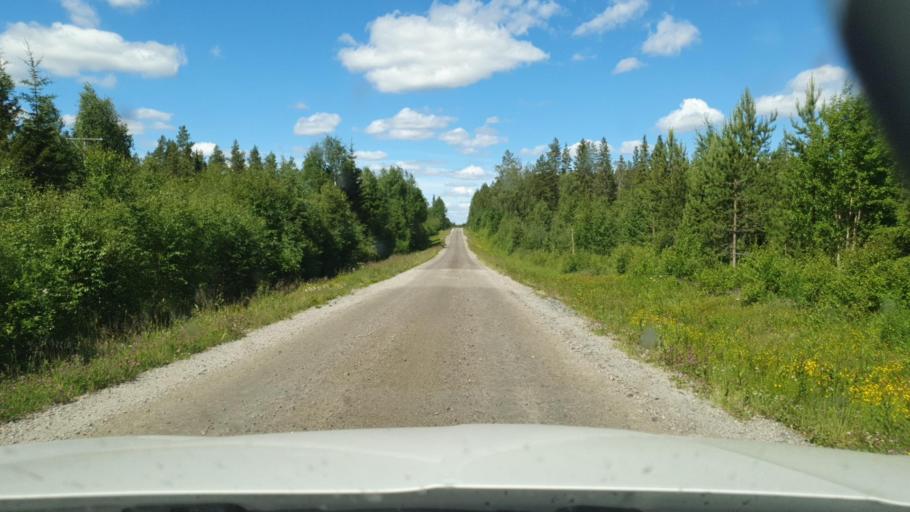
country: SE
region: Vaesterbotten
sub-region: Skelleftea Kommun
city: Byske
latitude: 65.1424
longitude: 21.1763
